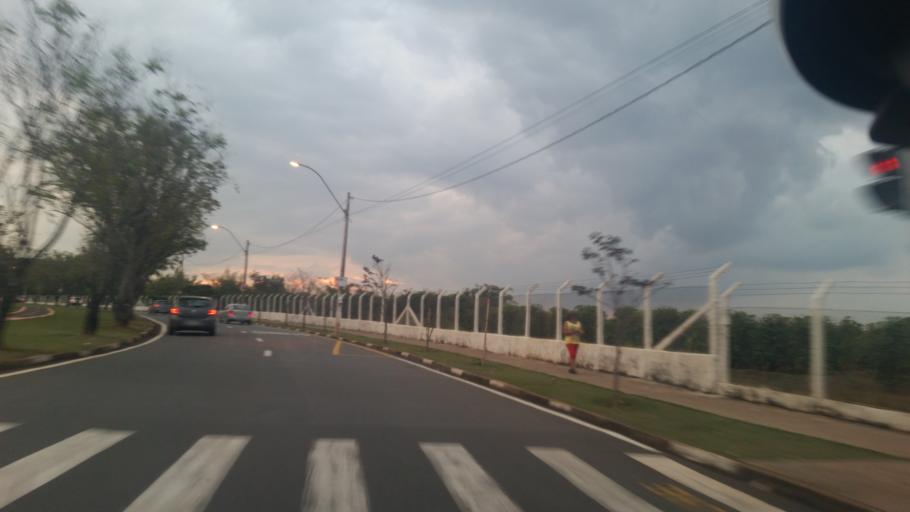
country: BR
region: Sao Paulo
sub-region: Campinas
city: Campinas
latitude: -22.8717
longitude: -47.0653
